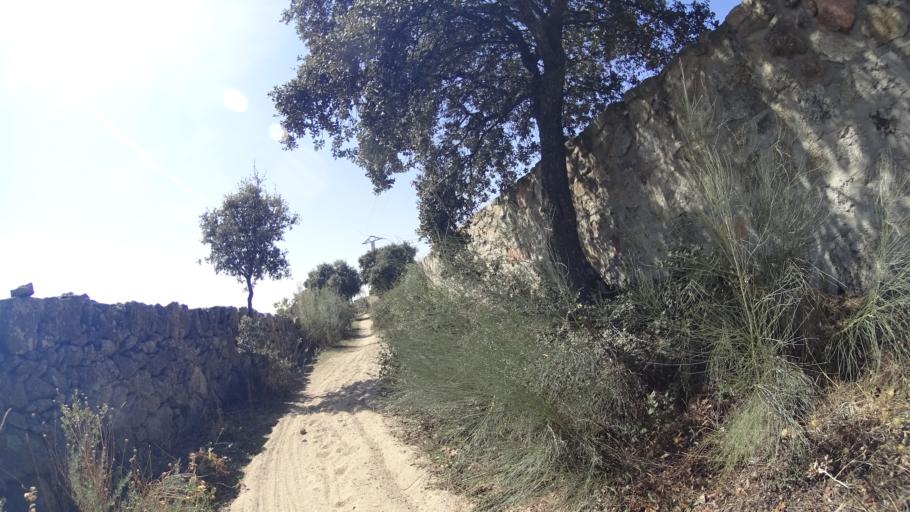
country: ES
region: Madrid
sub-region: Provincia de Madrid
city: Colmenarejo
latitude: 40.5695
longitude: -4.0264
